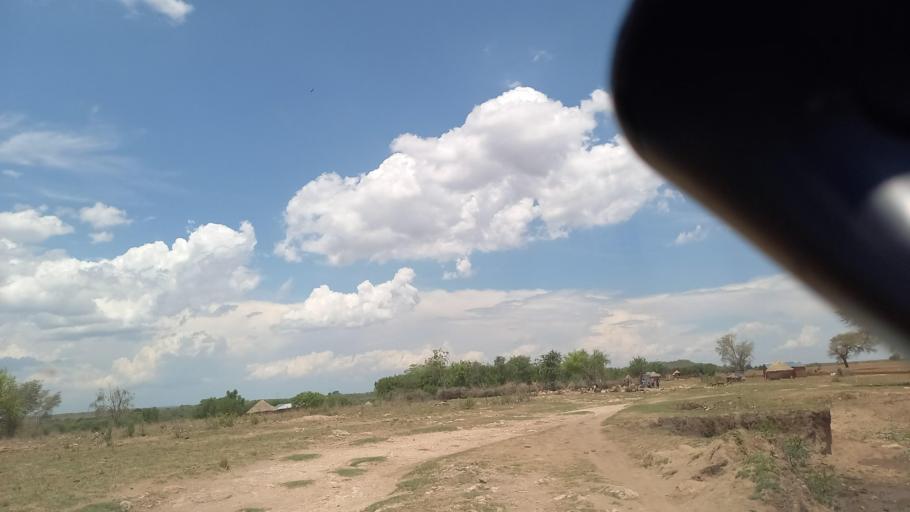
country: ZM
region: Southern
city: Mazabuka
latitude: -16.1096
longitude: 27.8229
